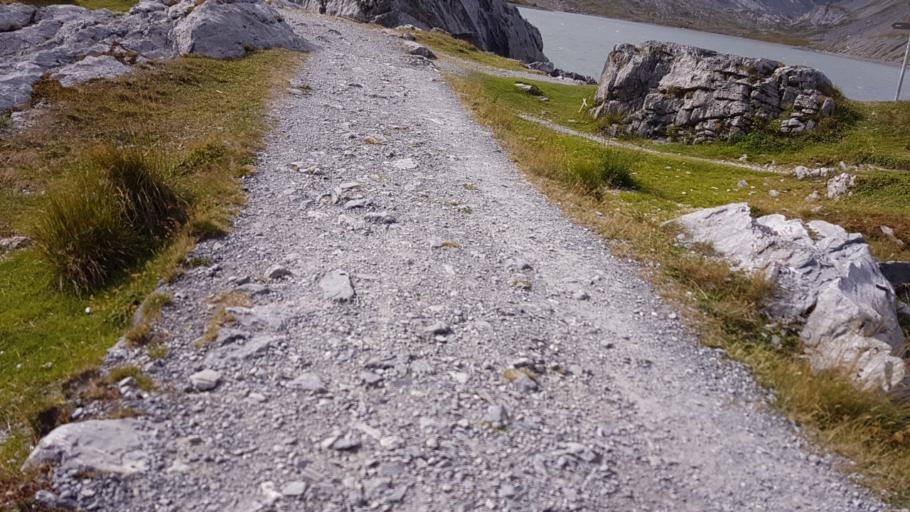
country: CH
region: Valais
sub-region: Leuk District
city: Leukerbad
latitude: 46.4191
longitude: 7.6235
